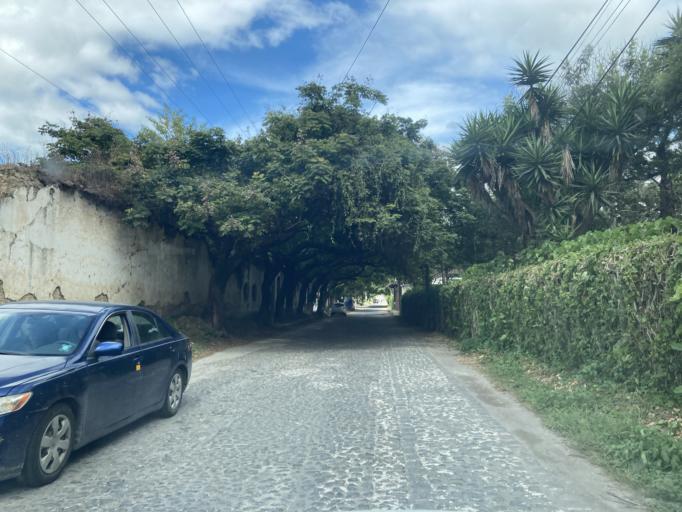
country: GT
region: Sacatepequez
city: Antigua Guatemala
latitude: 14.5486
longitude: -90.7342
